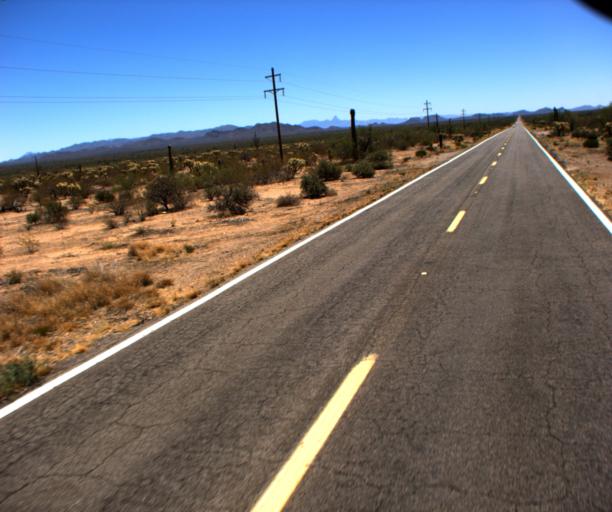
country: US
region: Arizona
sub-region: Pima County
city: Sells
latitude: 32.0994
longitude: -112.0650
